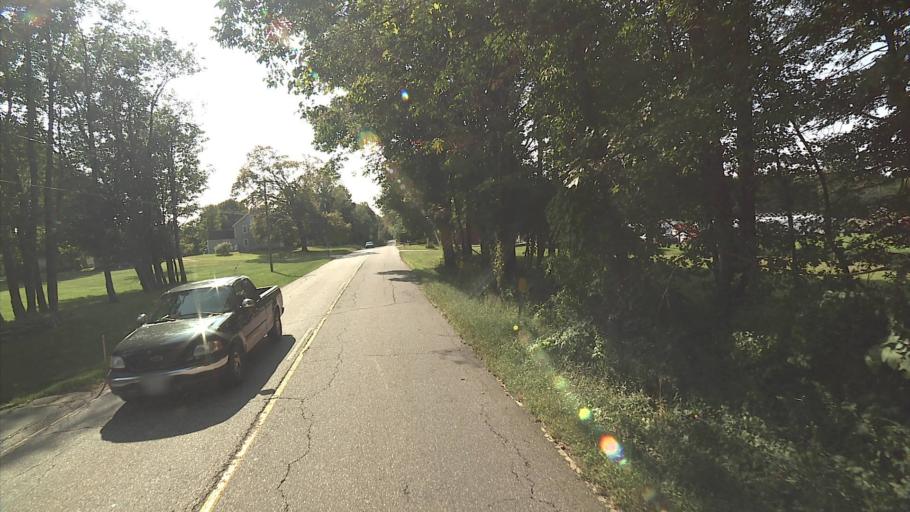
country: US
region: Connecticut
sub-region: Windham County
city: Willimantic
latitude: 41.6612
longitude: -72.2508
